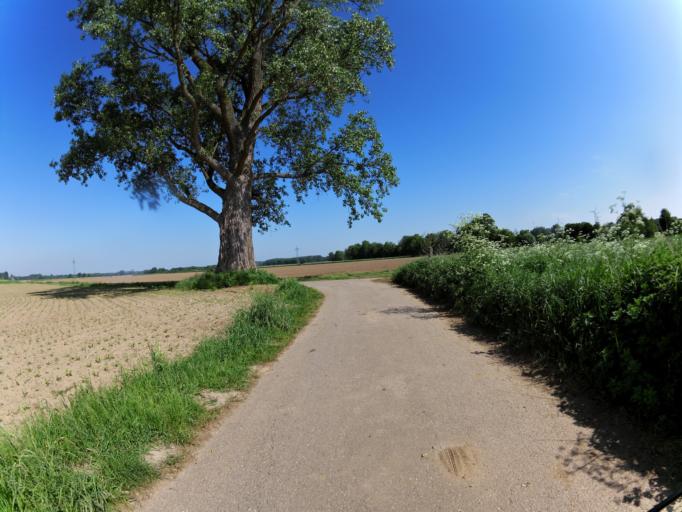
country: DE
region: North Rhine-Westphalia
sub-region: Regierungsbezirk Koln
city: Linnich
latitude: 50.9986
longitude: 6.2709
